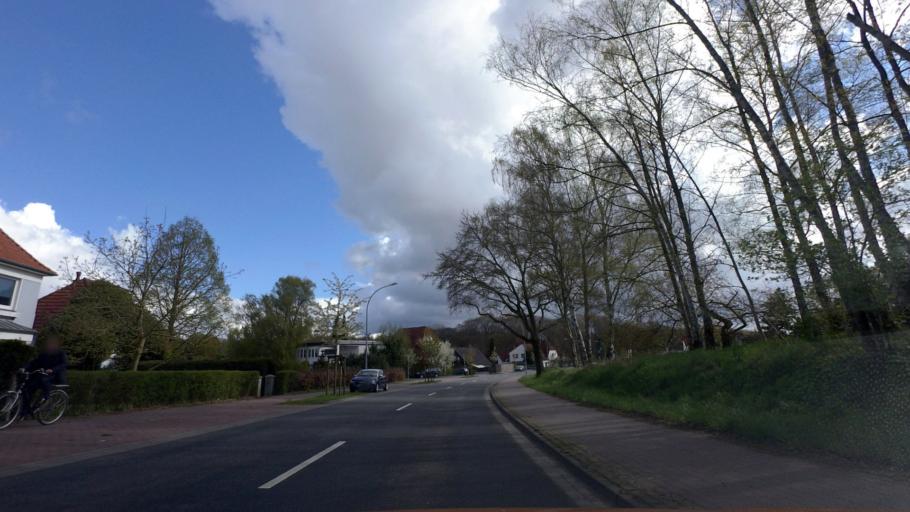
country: DE
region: Lower Saxony
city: Delmenhorst
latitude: 53.0492
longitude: 8.5897
